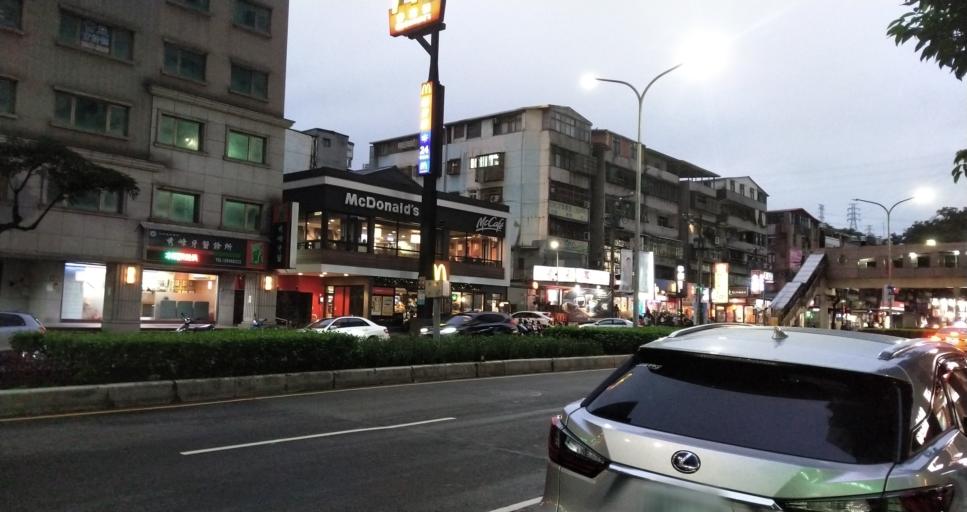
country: TW
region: Taiwan
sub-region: Keelung
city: Keelung
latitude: 25.0628
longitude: 121.6546
